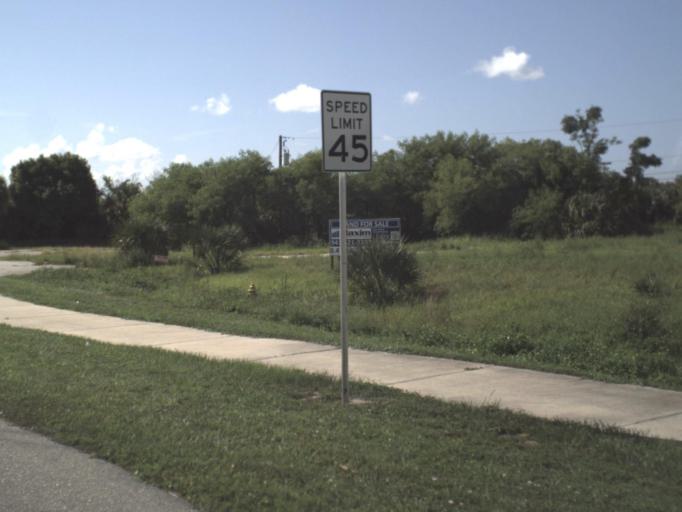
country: US
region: Florida
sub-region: Charlotte County
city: Charlotte Harbor
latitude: 26.9574
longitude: -82.0665
